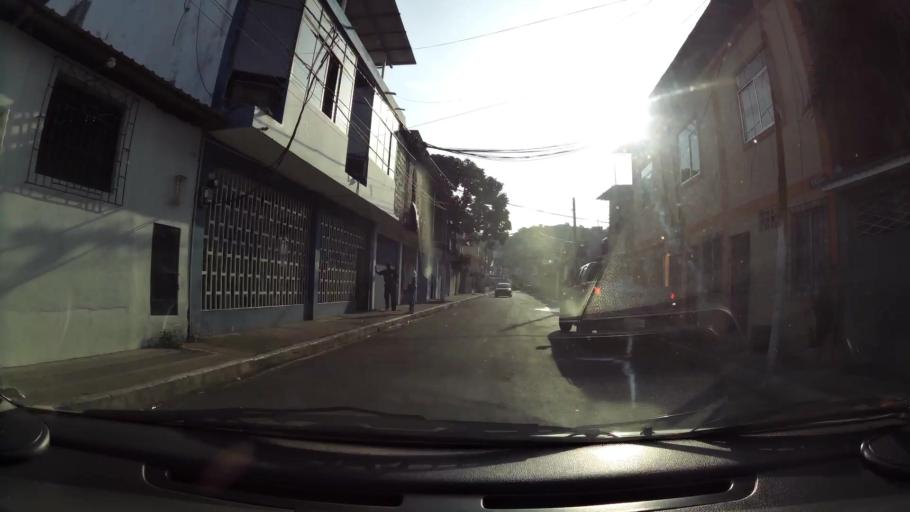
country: EC
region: Guayas
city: Eloy Alfaro
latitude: -2.1772
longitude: -79.8549
